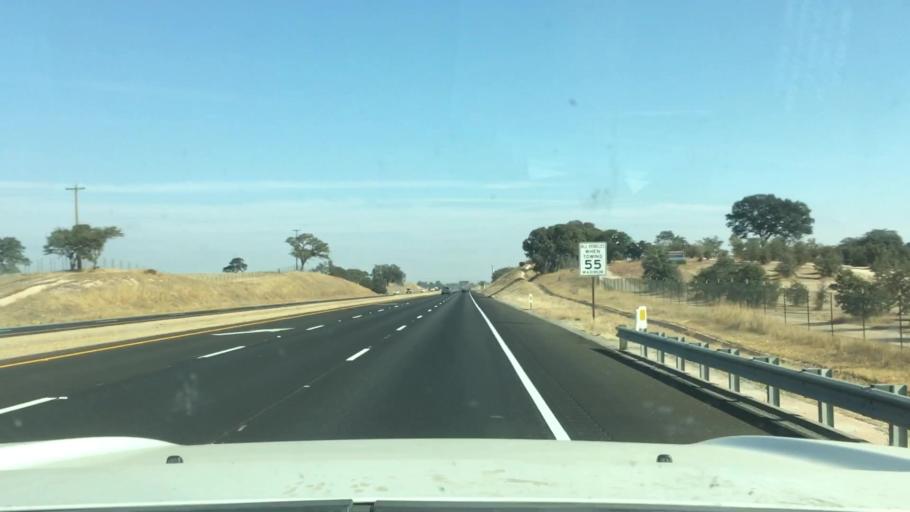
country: US
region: California
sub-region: San Luis Obispo County
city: Paso Robles
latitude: 35.6492
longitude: -120.6263
